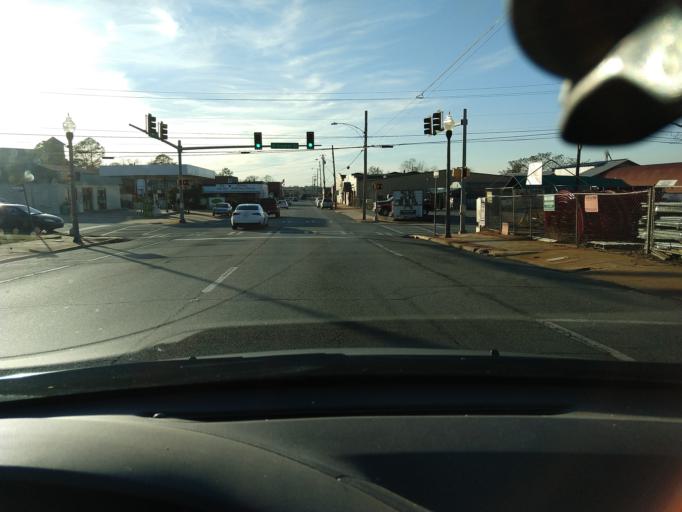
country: US
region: Georgia
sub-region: Sumter County
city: Americus
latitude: 32.0733
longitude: -84.2360
